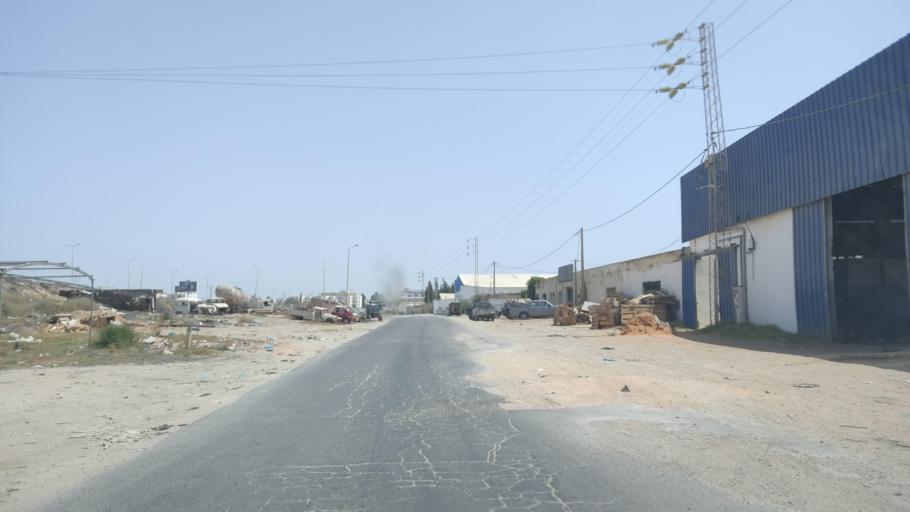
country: TN
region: Safaqis
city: Sfax
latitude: 34.7060
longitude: 10.7220
